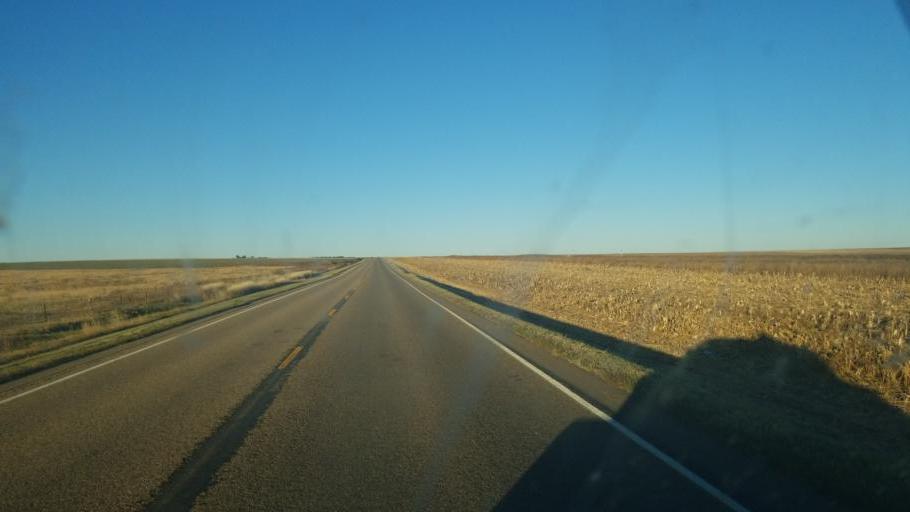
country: US
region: Colorado
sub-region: Cheyenne County
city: Cheyenne Wells
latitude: 38.8114
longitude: -102.3951
